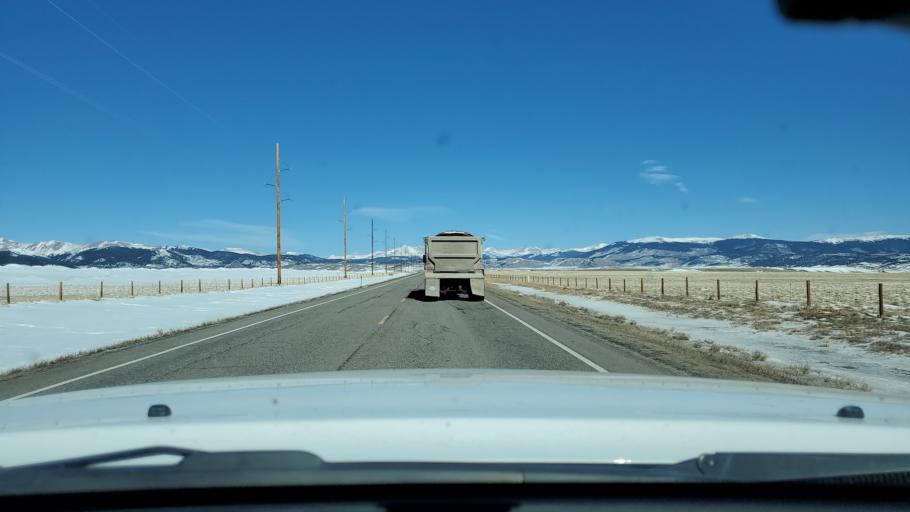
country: US
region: Colorado
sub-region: Park County
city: Fairplay
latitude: 39.3197
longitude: -105.8777
